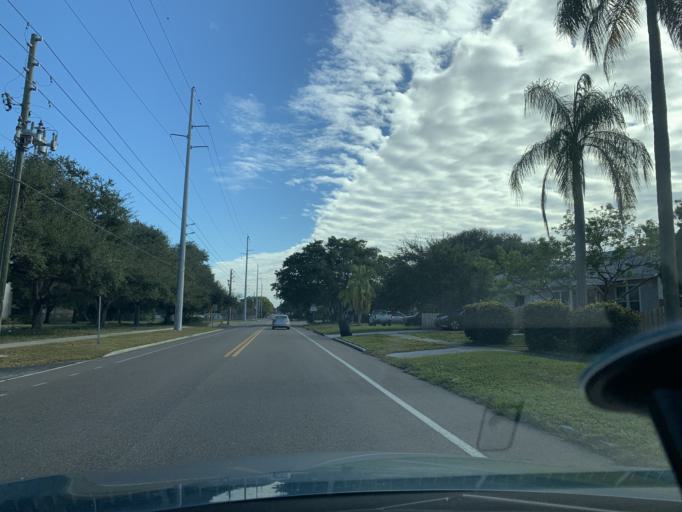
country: US
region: Florida
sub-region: Pinellas County
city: Saint Petersburg
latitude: 27.7846
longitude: -82.6766
